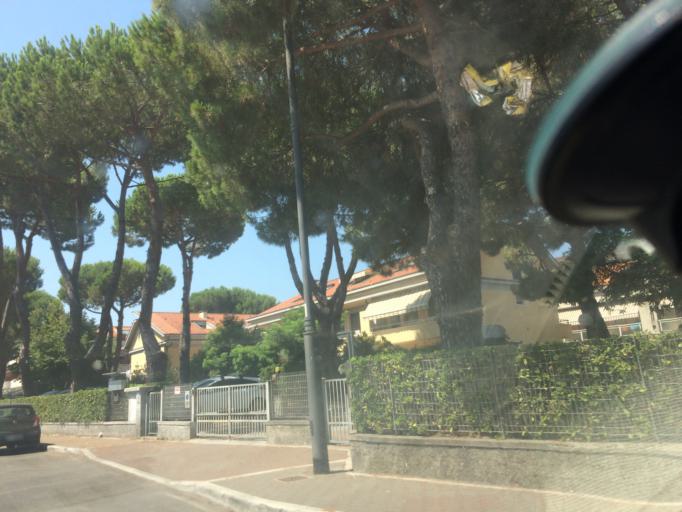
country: IT
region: Tuscany
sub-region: Provincia di Massa-Carrara
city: Massa
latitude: 44.0143
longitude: 10.0958
